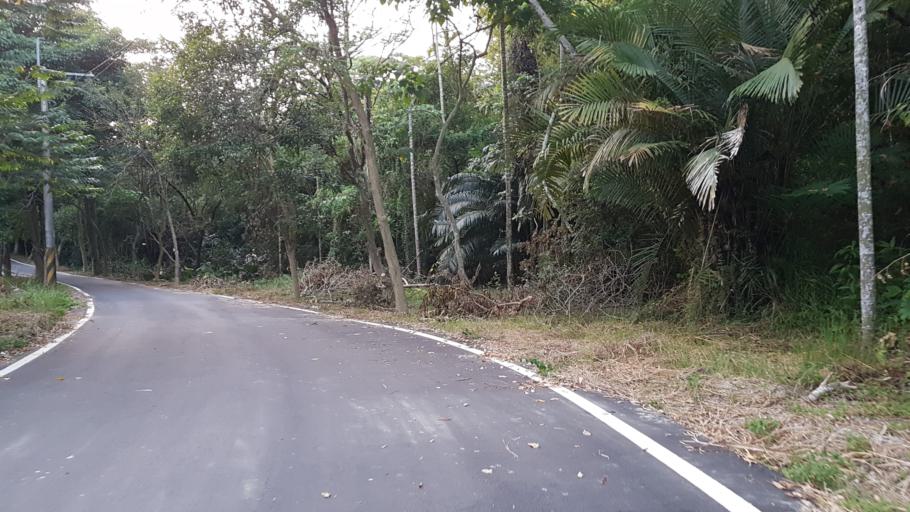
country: TW
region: Taiwan
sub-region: Chiayi
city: Jiayi Shi
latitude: 23.3623
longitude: 120.4677
